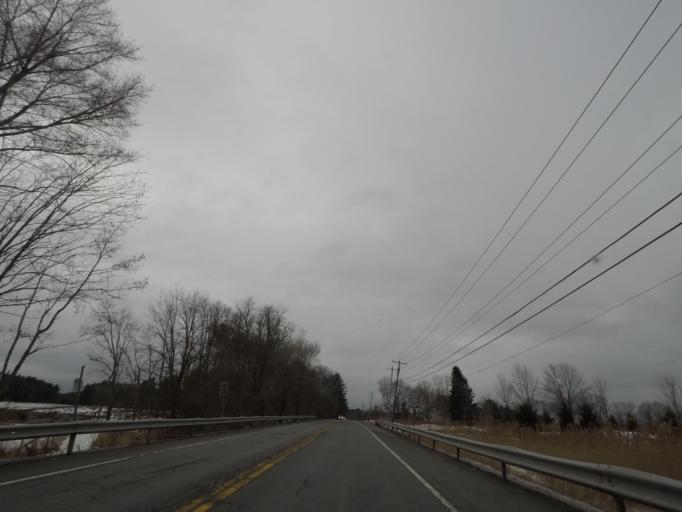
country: US
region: New York
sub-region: Schenectady County
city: Rotterdam
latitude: 42.7267
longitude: -73.9635
